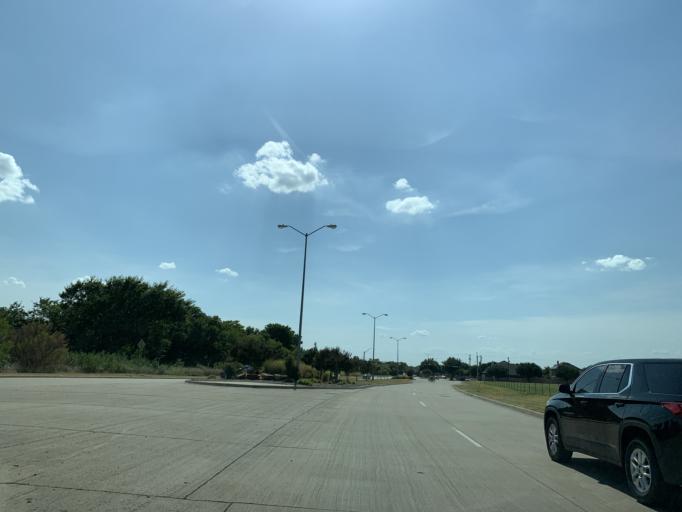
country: US
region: Texas
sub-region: Dallas County
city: Cedar Hill
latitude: 32.6439
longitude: -97.0118
